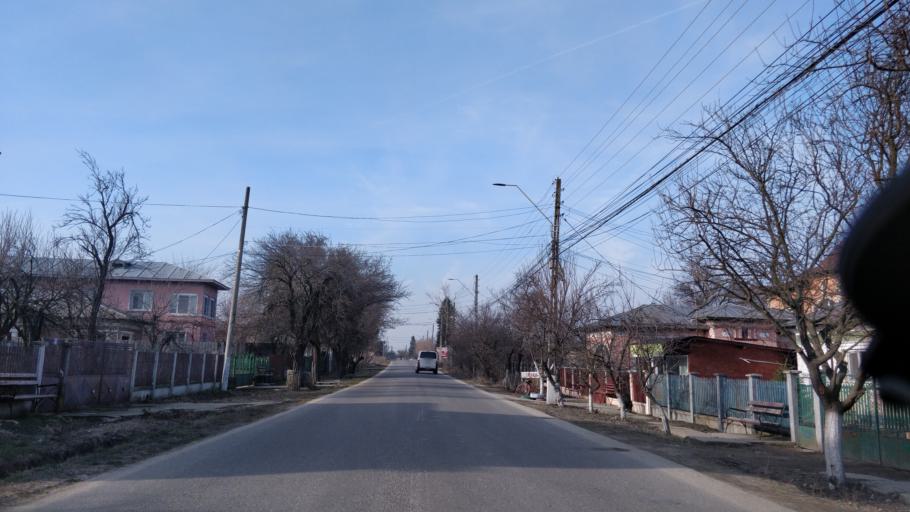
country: RO
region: Giurgiu
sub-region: Comuna Ulmi
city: Ulmi
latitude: 44.4900
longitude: 25.7800
